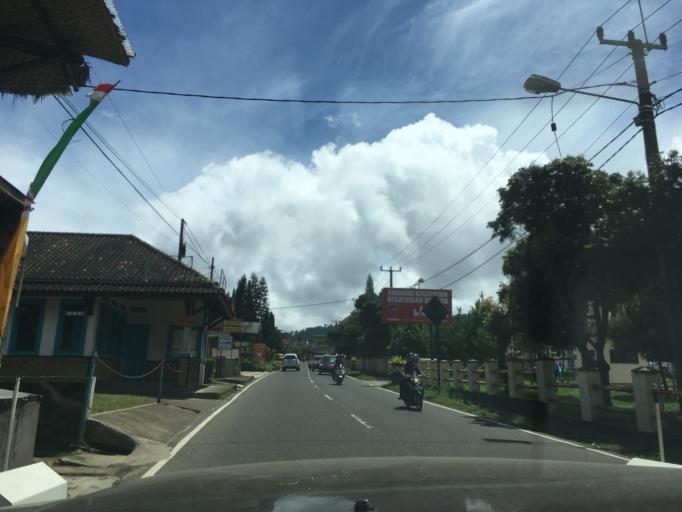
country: ID
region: West Java
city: Lembang
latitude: -6.7970
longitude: 107.6534
